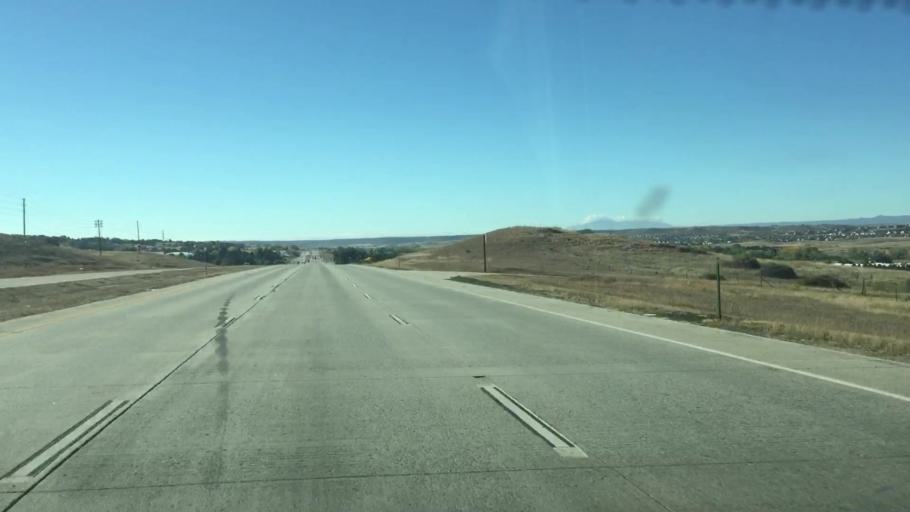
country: US
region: Colorado
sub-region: Douglas County
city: The Pinery
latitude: 39.4664
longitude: -104.7589
